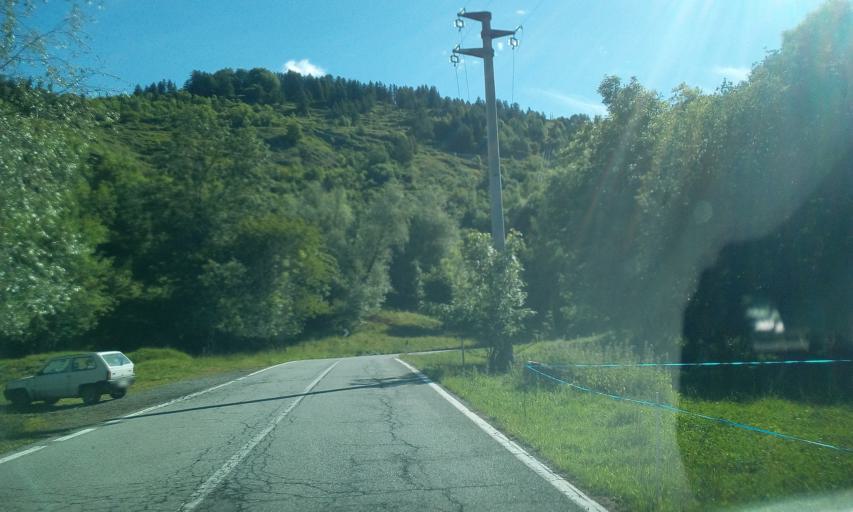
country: IT
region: Aosta Valley
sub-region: Valle d'Aosta
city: Emarese
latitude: 45.7510
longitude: 7.6872
